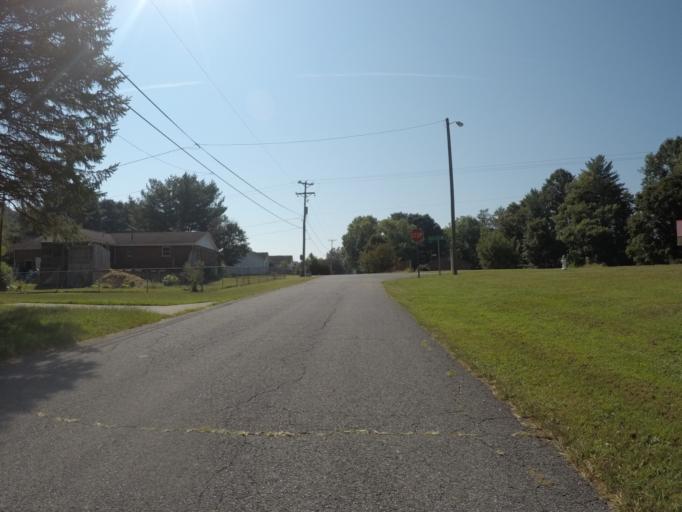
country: US
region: West Virginia
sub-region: Cabell County
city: Barboursville
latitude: 38.3739
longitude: -82.2771
